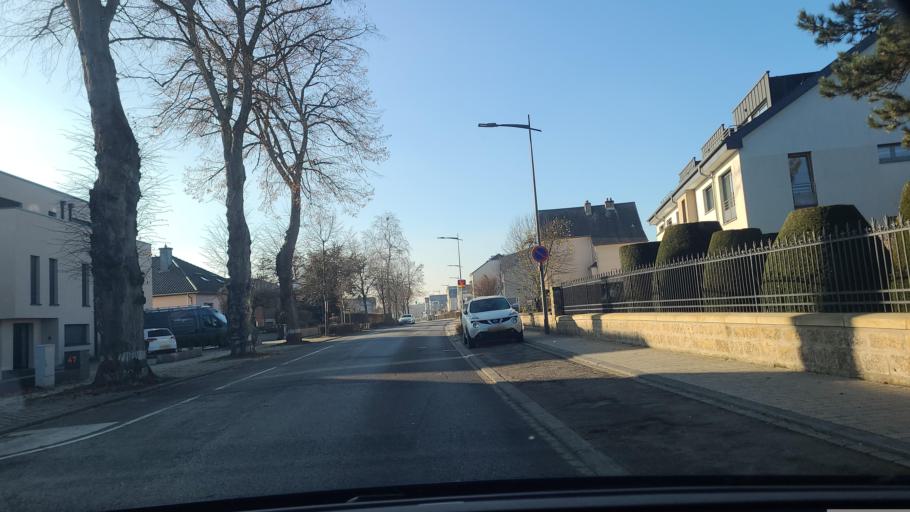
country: LU
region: Luxembourg
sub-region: Canton de Capellen
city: Mamer
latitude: 49.6244
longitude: 6.0144
